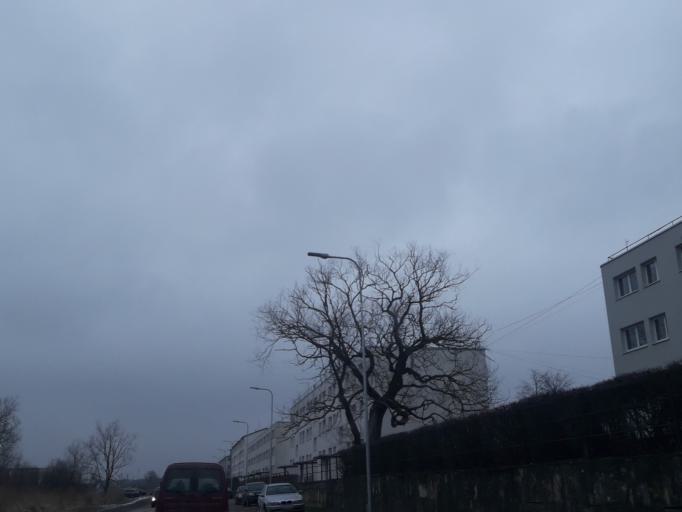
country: EE
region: Saare
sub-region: Kuressaare linn
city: Kuressaare
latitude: 58.2602
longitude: 22.4802
